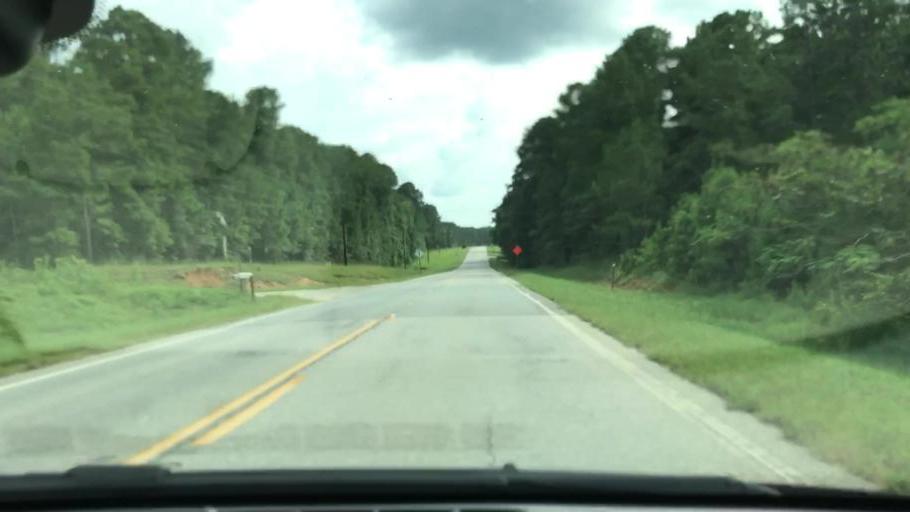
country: US
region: Georgia
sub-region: Clay County
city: Fort Gaines
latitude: 31.6404
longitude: -85.0441
